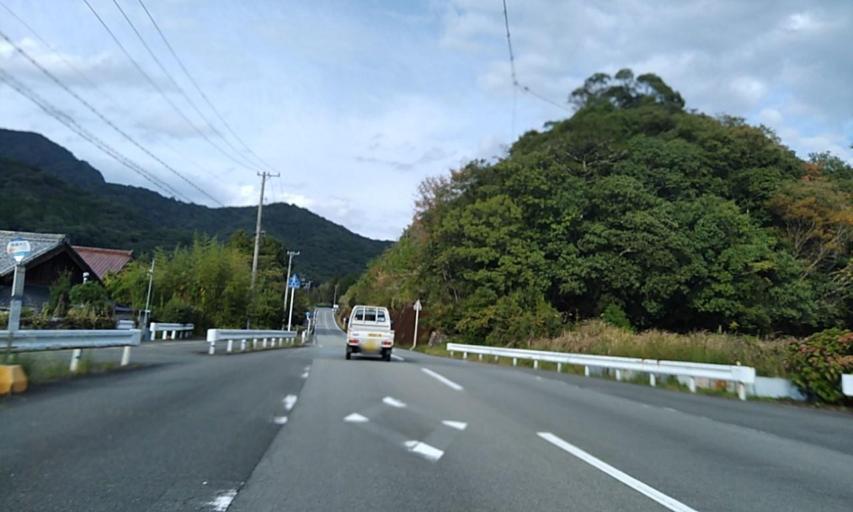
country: JP
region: Mie
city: Ise
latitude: 34.2955
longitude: 136.6020
